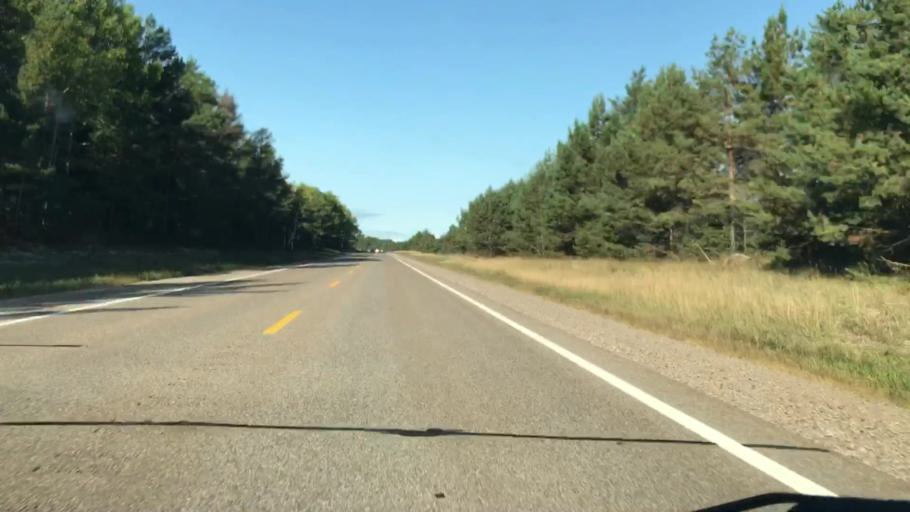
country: US
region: Michigan
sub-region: Mackinac County
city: Saint Ignace
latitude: 46.3584
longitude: -84.8688
